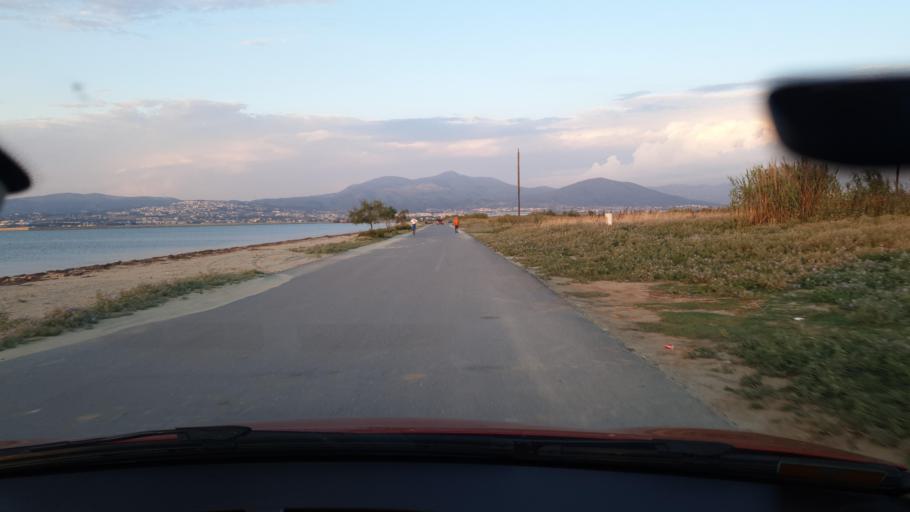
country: GR
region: Central Macedonia
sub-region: Nomos Thessalonikis
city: Peraia
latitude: 40.5136
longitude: 22.9375
